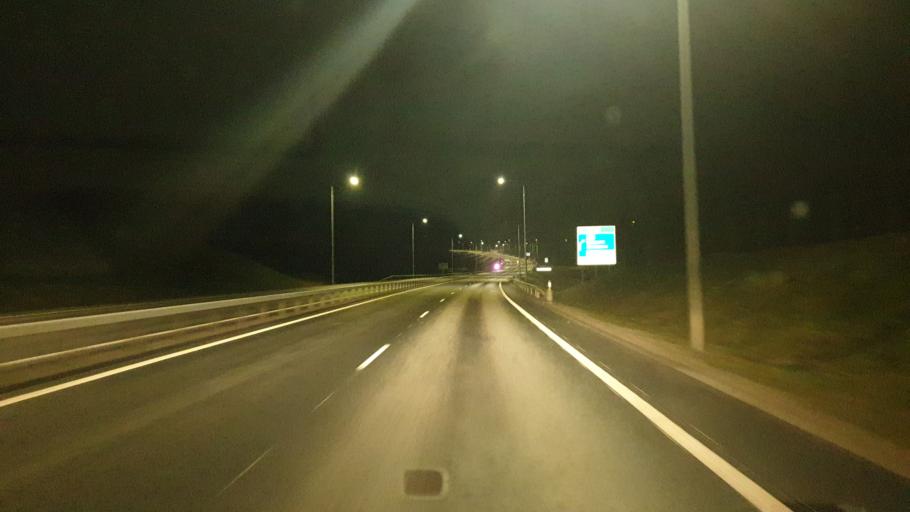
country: FI
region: Central Finland
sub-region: AEaenekoski
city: AEaenekoski
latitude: 62.6005
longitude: 25.6889
